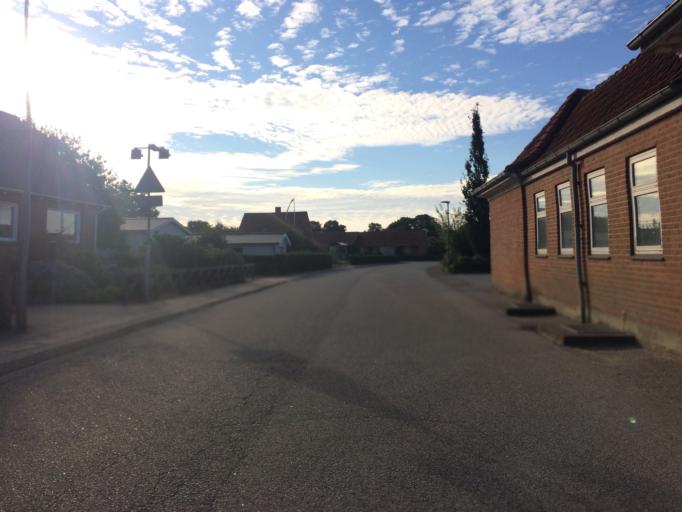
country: DK
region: Central Jutland
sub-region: Holstebro Kommune
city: Vinderup
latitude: 56.6120
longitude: 8.8818
